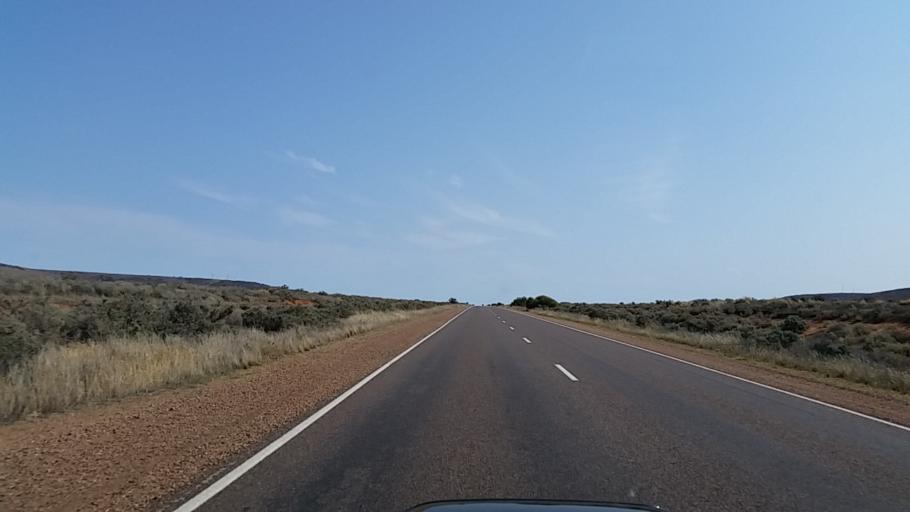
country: AU
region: South Australia
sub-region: Port Augusta
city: Port Augusta West
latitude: -32.5891
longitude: 137.6107
